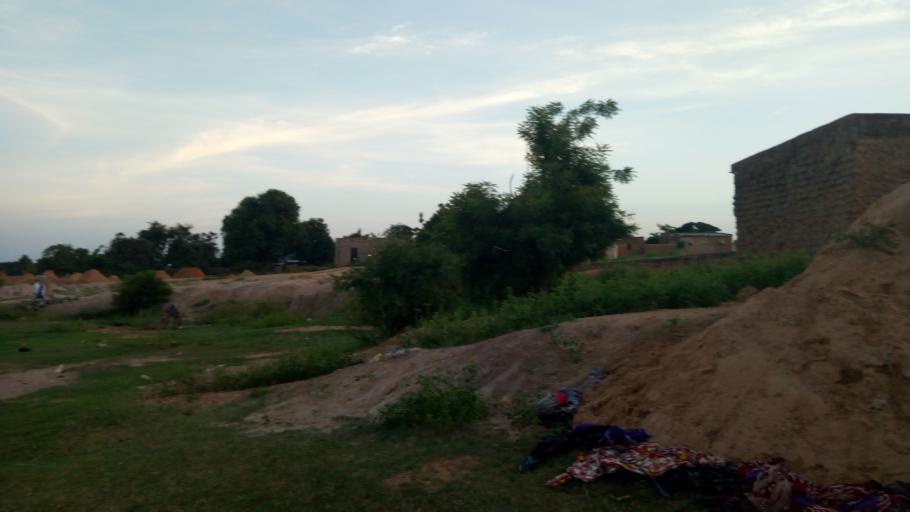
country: ML
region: Sikasso
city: Koutiala
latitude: 12.4014
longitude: -5.4465
